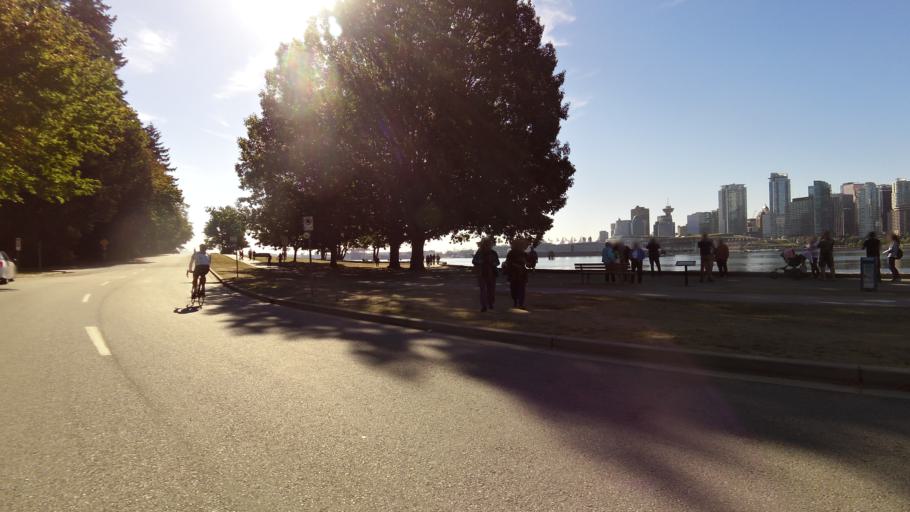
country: CA
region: British Columbia
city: West End
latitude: 49.2986
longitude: -123.1213
